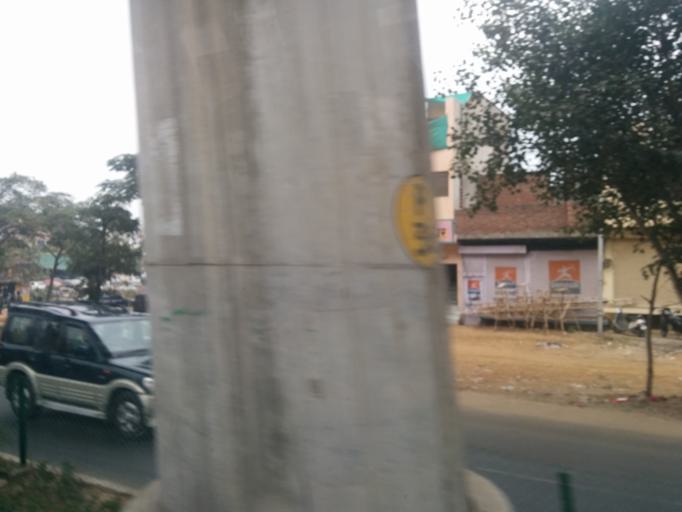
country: IN
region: Rajasthan
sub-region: Jaipur
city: Jaipur
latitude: 26.8801
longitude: 75.7574
